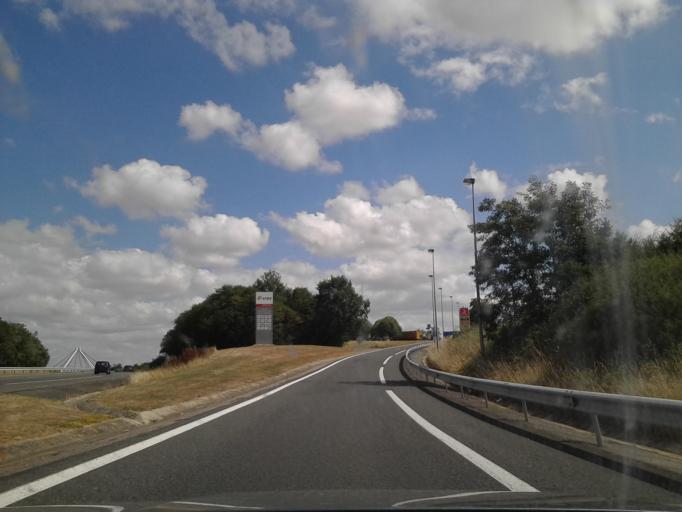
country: FR
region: Centre
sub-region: Departement du Cher
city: Orval
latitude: 46.7560
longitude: 2.4119
